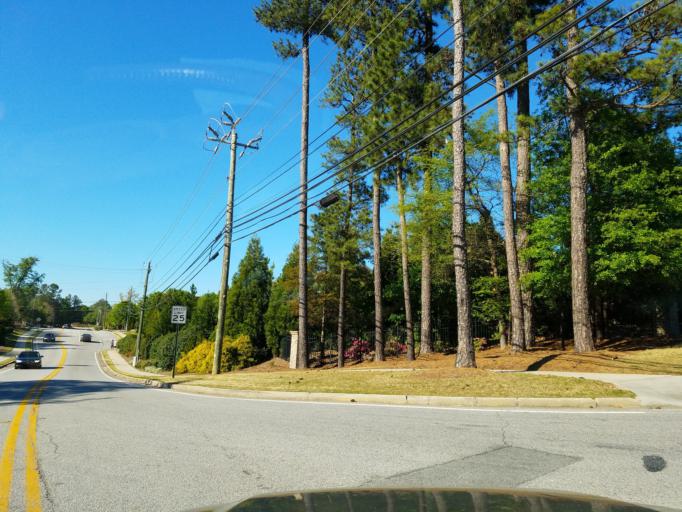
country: US
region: Georgia
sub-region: Cobb County
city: Vinings
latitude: 33.8315
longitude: -84.4824
